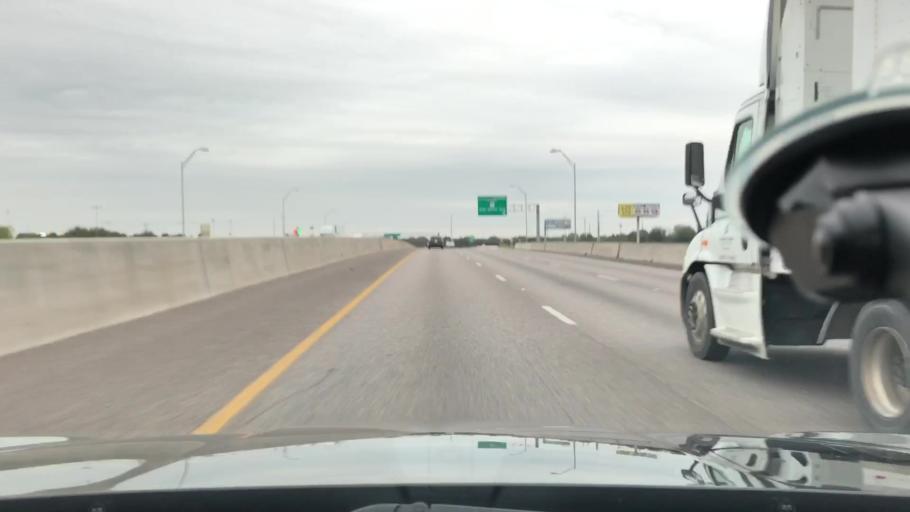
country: US
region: Texas
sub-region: McLennan County
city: Northcrest
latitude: 31.6387
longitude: -97.0962
